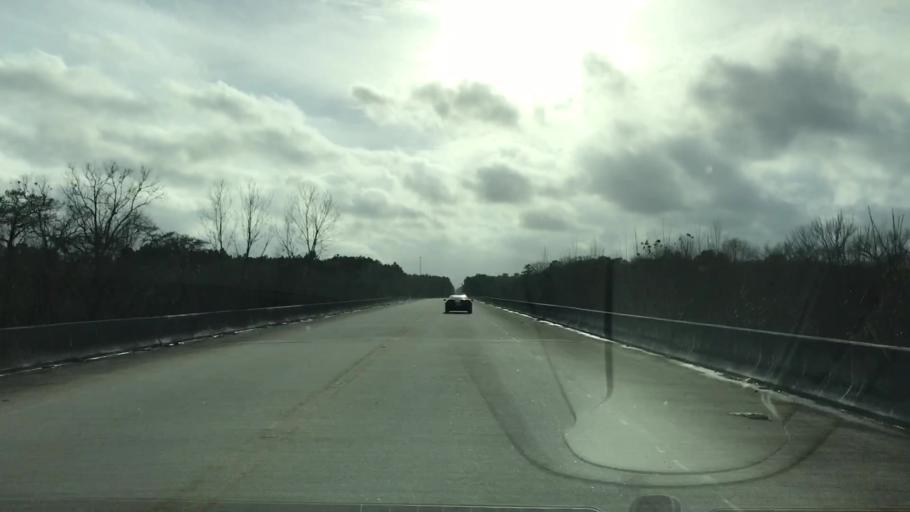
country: US
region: South Carolina
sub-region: Williamsburg County
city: Andrews
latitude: 33.3063
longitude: -79.6768
